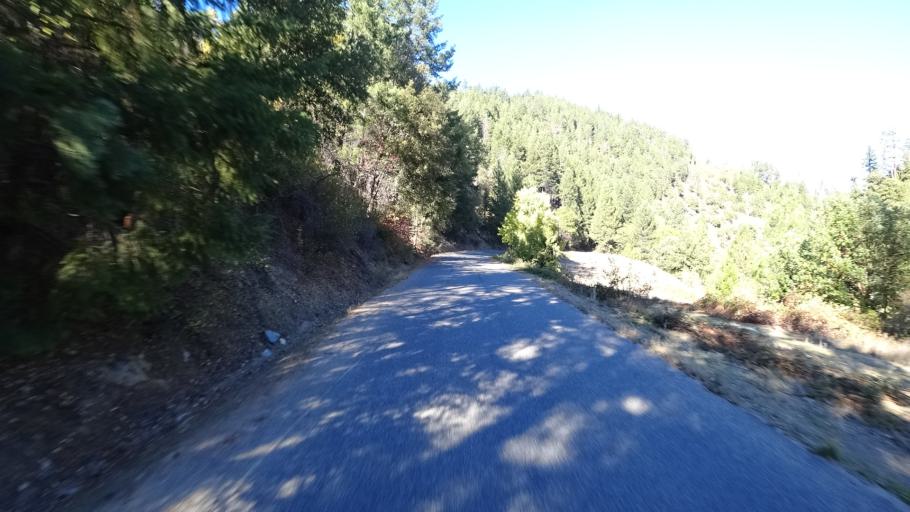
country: US
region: California
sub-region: Humboldt County
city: Willow Creek
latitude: 41.2879
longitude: -123.2515
